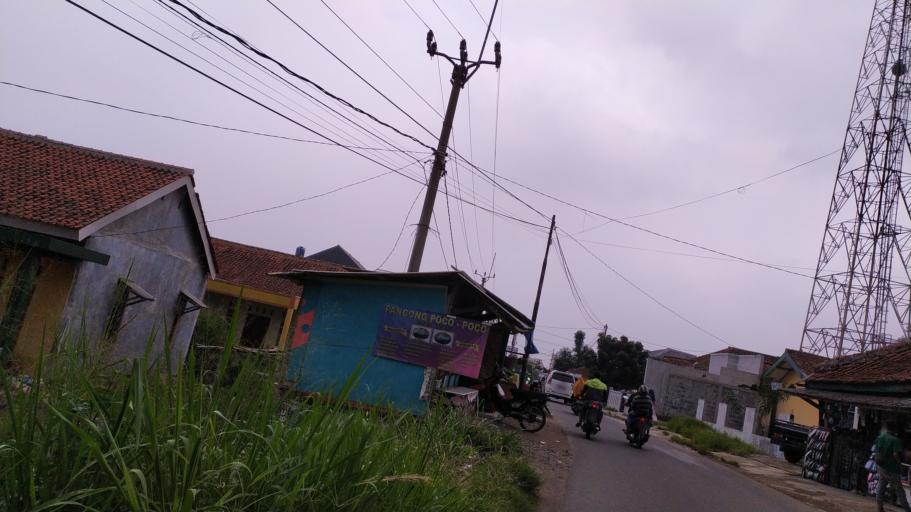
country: ID
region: West Java
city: Ciampea
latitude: -6.6049
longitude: 106.7014
